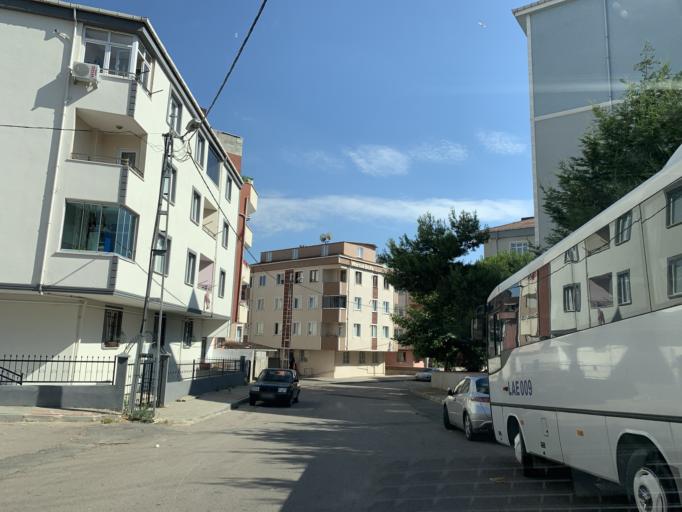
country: TR
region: Istanbul
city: Pendik
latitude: 40.8876
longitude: 29.2696
